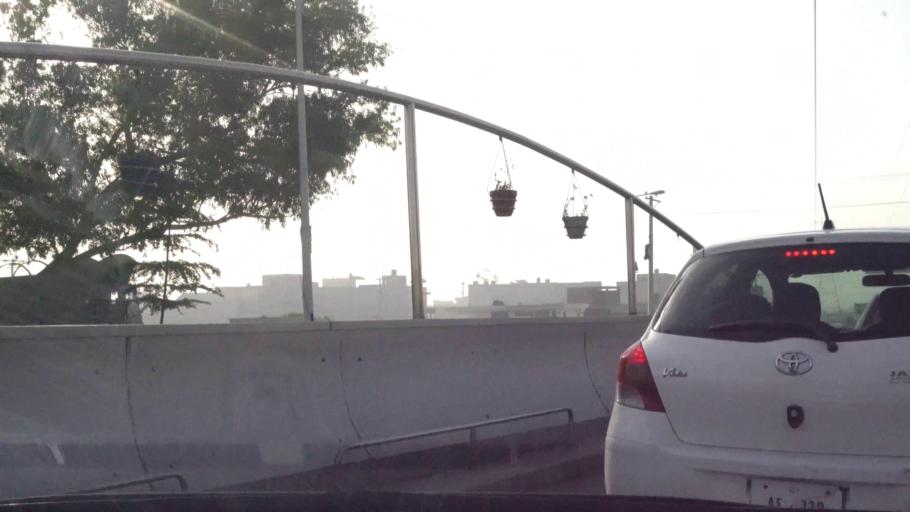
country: PK
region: Punjab
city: Khurrianwala
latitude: 31.4607
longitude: 73.1753
